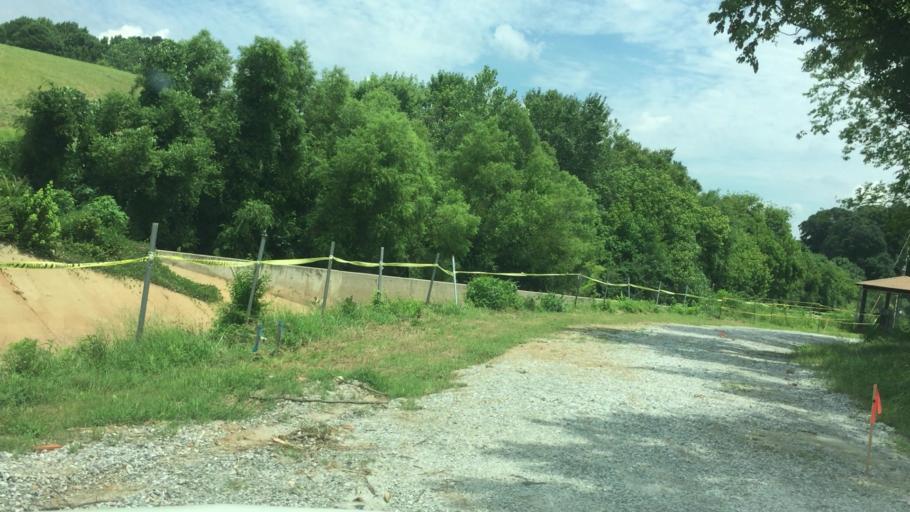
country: US
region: Georgia
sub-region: Fulton County
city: Atlanta
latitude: 33.7192
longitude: -84.3617
